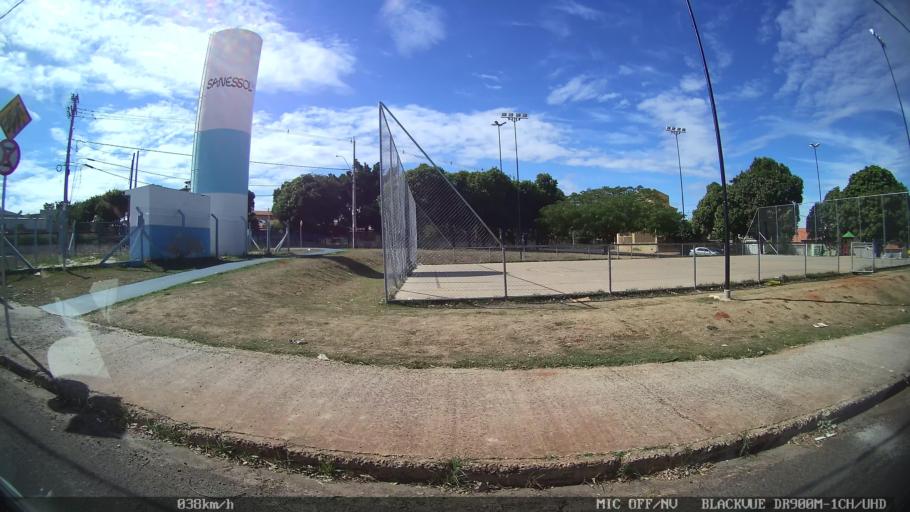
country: BR
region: Sao Paulo
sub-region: Bady Bassitt
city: Bady Bassitt
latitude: -20.8230
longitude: -49.4943
